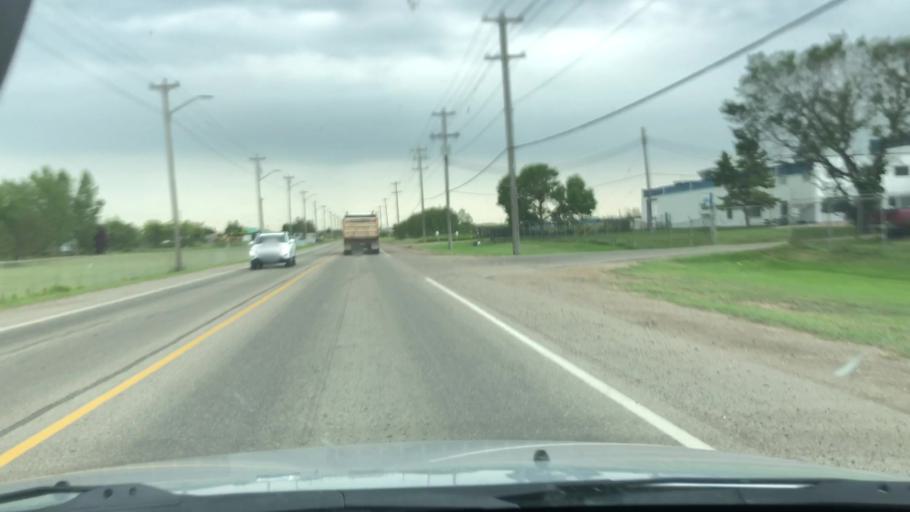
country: CA
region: Alberta
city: Sherwood Park
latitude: 53.5260
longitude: -113.3939
